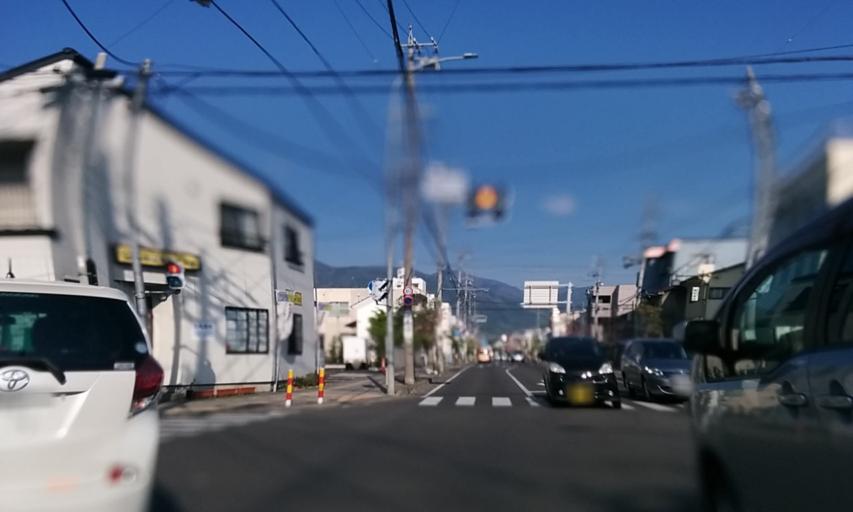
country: JP
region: Nagano
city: Matsumoto
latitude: 36.2389
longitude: 137.9748
